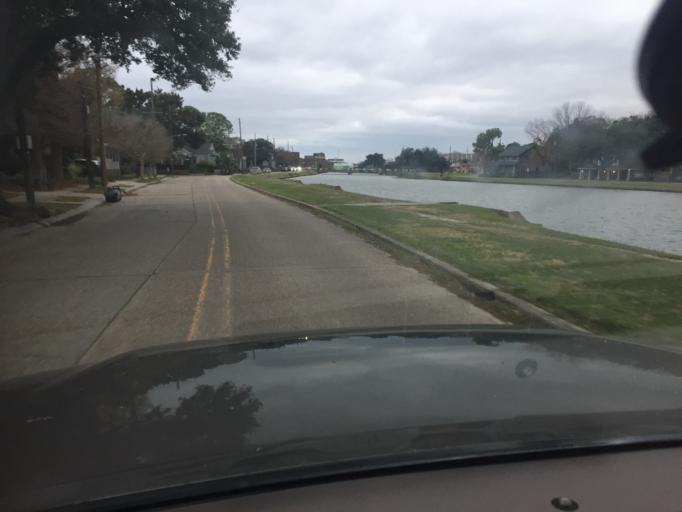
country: US
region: Louisiana
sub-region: Orleans Parish
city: New Orleans
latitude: 29.9794
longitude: -90.0874
